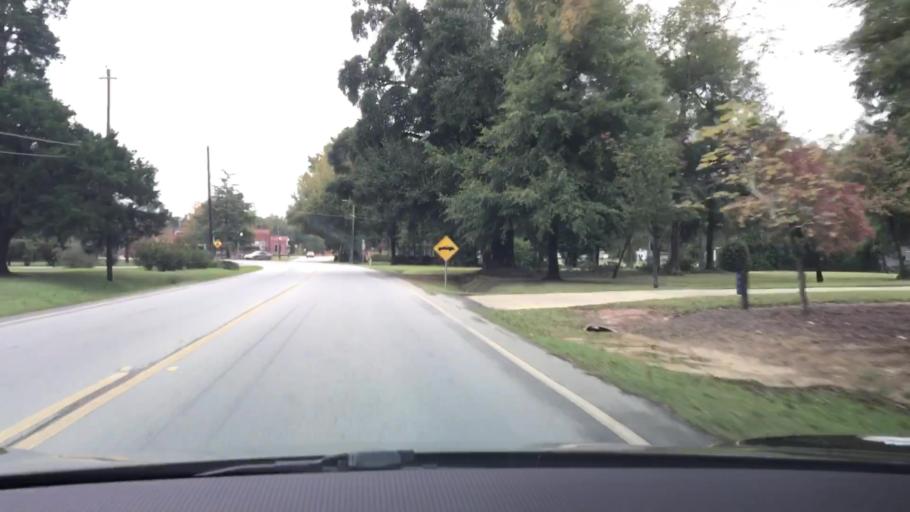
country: US
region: Georgia
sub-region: Jefferson County
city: Wrens
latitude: 33.2177
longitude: -82.4670
